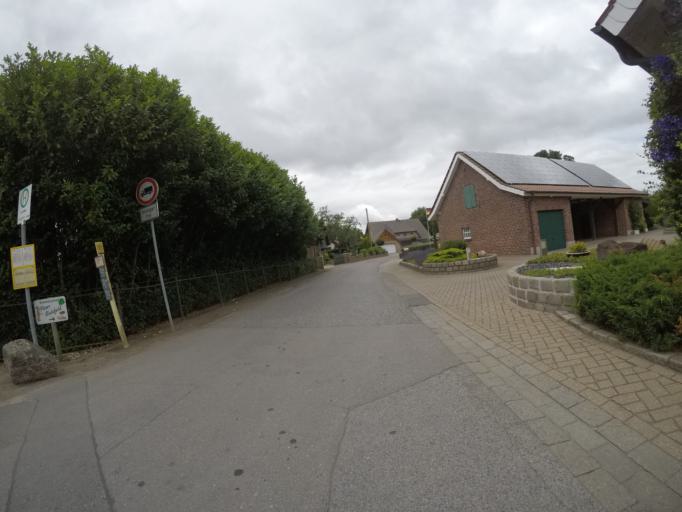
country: DE
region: North Rhine-Westphalia
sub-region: Regierungsbezirk Dusseldorf
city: Hamminkeln
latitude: 51.7659
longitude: 6.6046
